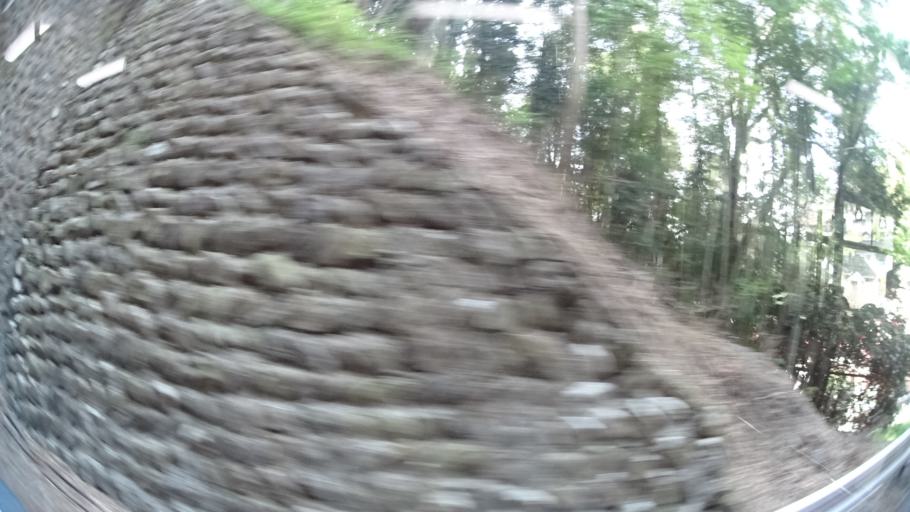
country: JP
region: Iwate
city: Ofunato
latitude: 38.9080
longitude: 141.5683
